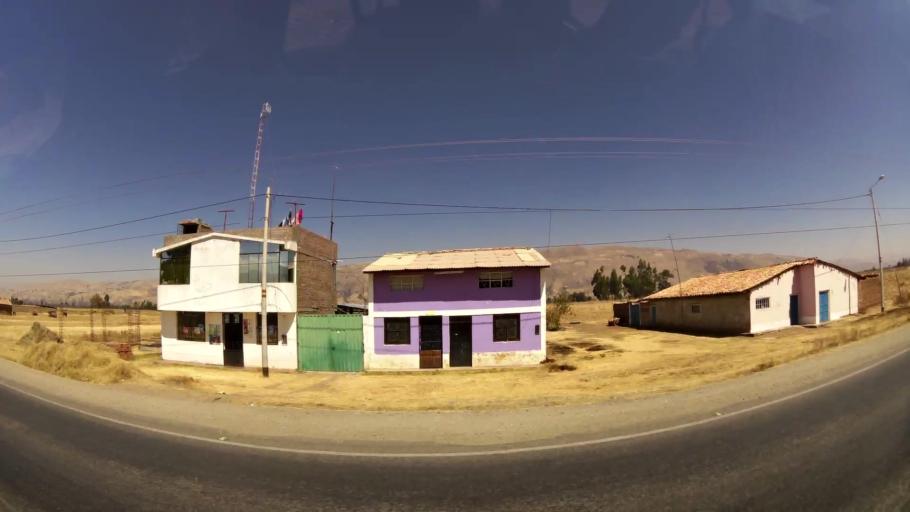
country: PE
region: Junin
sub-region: Provincia de Jauja
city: San Lorenzo
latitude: -11.8395
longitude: -75.3913
